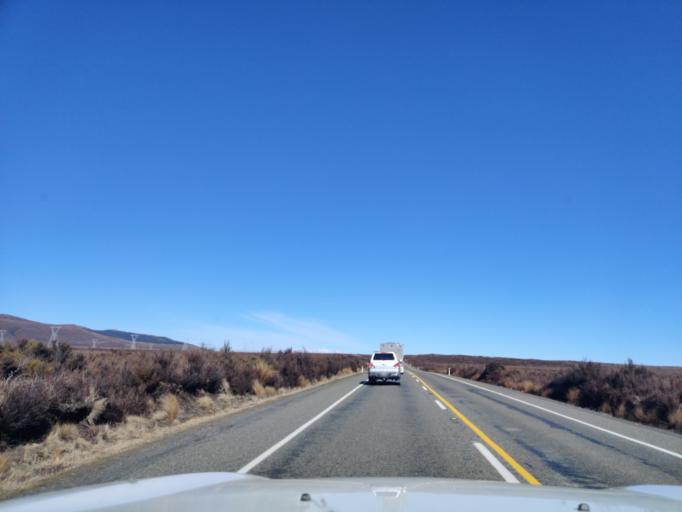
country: NZ
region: Manawatu-Wanganui
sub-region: Ruapehu District
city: Waiouru
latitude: -39.2554
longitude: 175.7356
